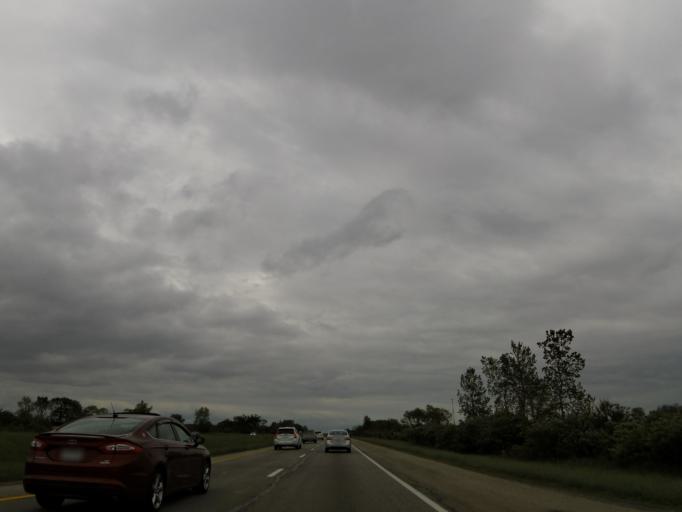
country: US
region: Ohio
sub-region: Madison County
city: Mount Sterling
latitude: 39.8005
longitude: -83.2139
